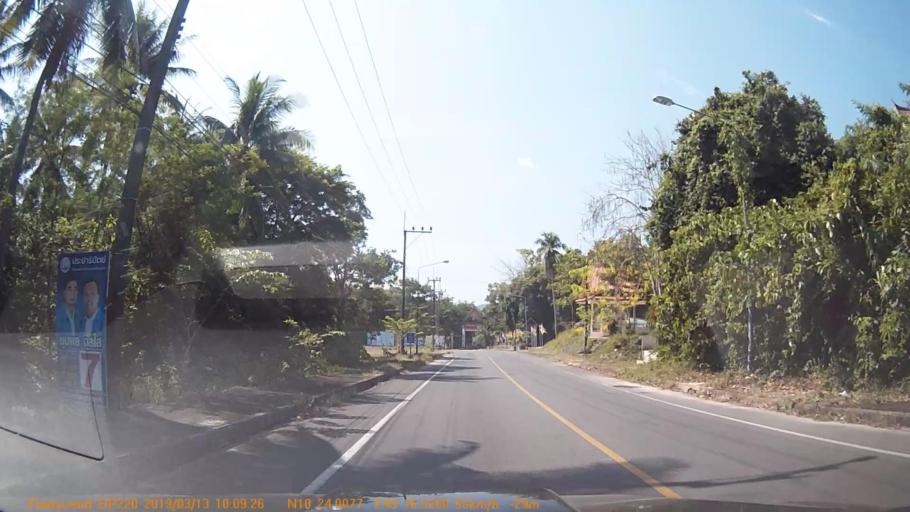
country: TH
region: Chumphon
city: Chumphon
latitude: 10.4003
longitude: 99.2754
